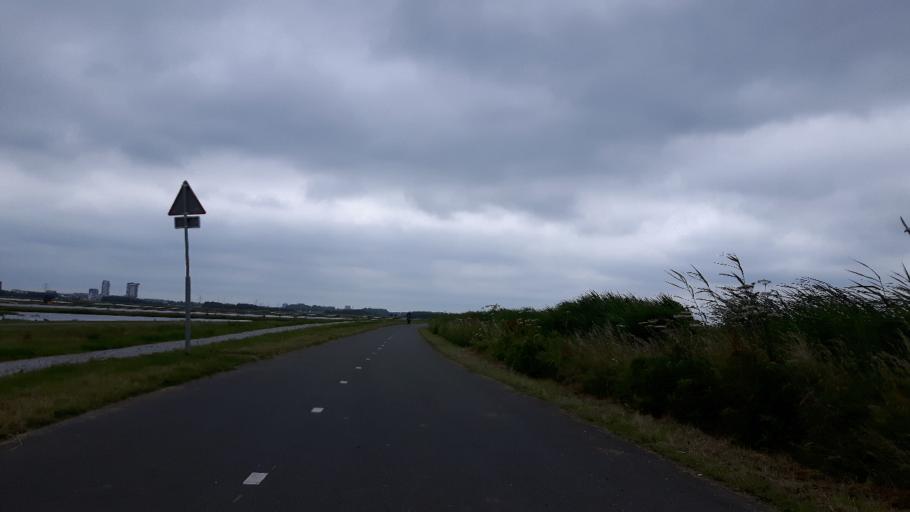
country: NL
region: South Holland
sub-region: Gemeente Lansingerland
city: Bleiswijk
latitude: 51.9999
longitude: 4.5572
